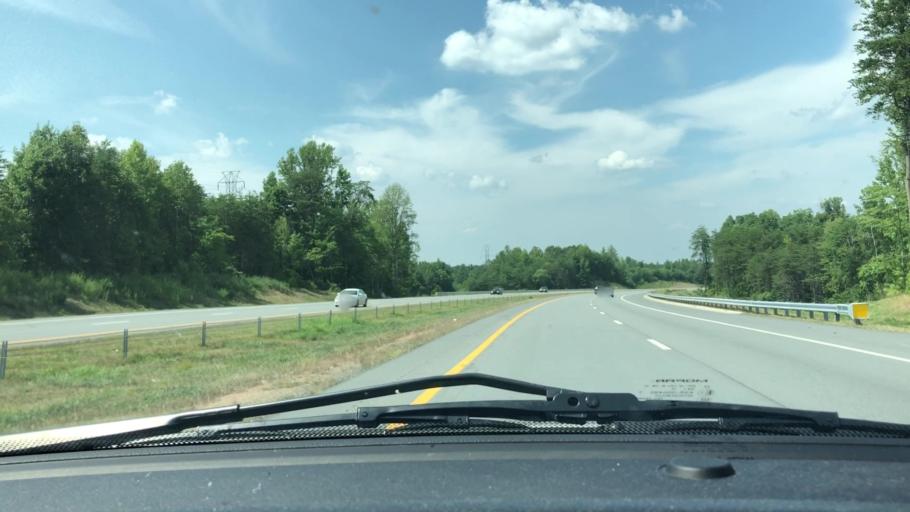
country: US
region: North Carolina
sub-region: Guilford County
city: Oak Ridge
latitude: 36.1551
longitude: -79.9593
